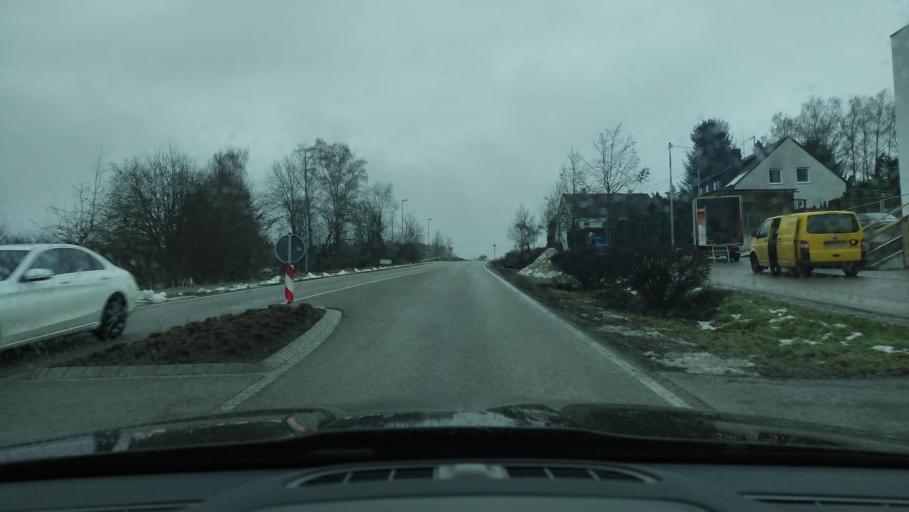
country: DE
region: Bavaria
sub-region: Swabia
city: Weissenhorn
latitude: 48.2967
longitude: 10.1714
